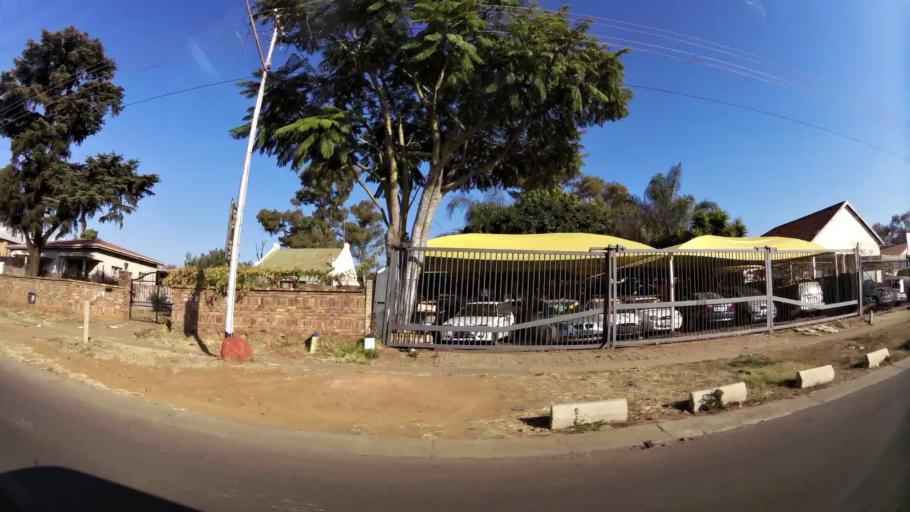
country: ZA
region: Gauteng
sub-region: City of Tshwane Metropolitan Municipality
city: Pretoria
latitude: -25.7432
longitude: 28.1654
